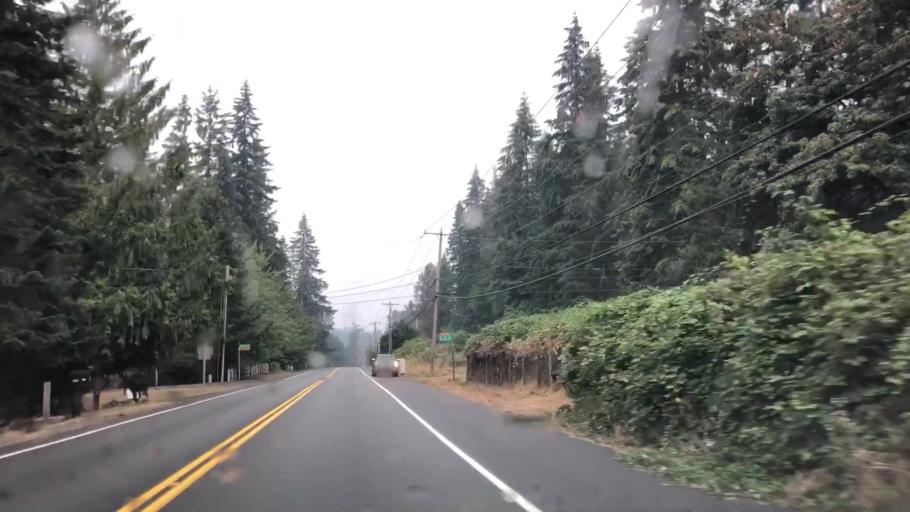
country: US
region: Washington
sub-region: King County
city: Cottage Lake
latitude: 47.7424
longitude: -122.0490
